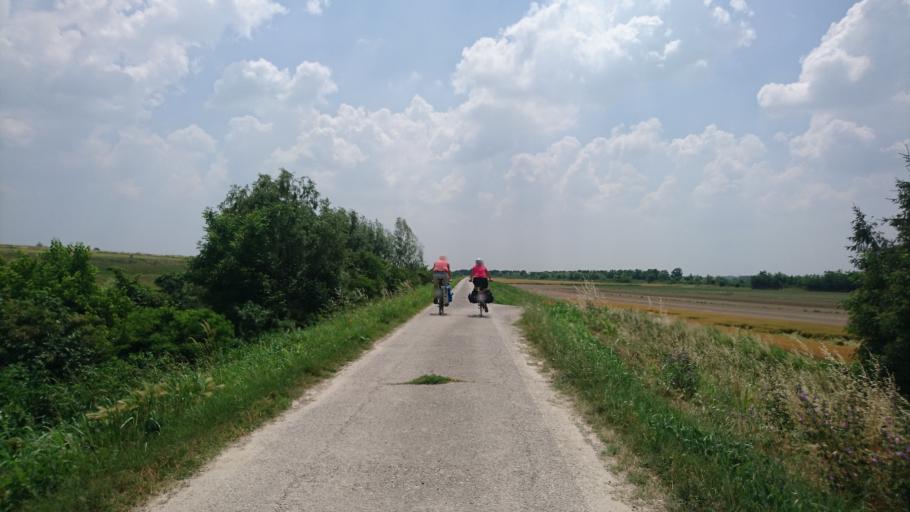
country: IT
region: Veneto
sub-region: Provincia di Venezia
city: Valli
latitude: 45.2189
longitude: 12.1623
